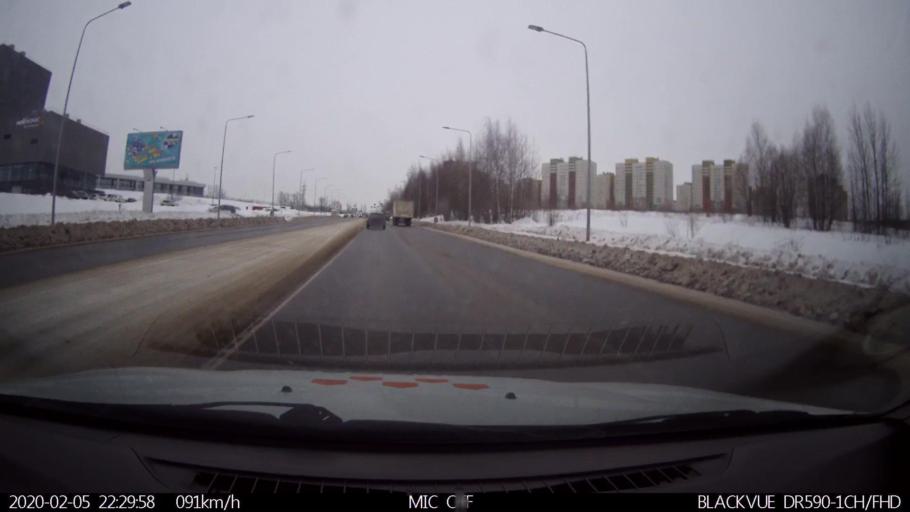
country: RU
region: Nizjnij Novgorod
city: Imeni Stepana Razina
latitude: 54.7456
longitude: 44.1521
